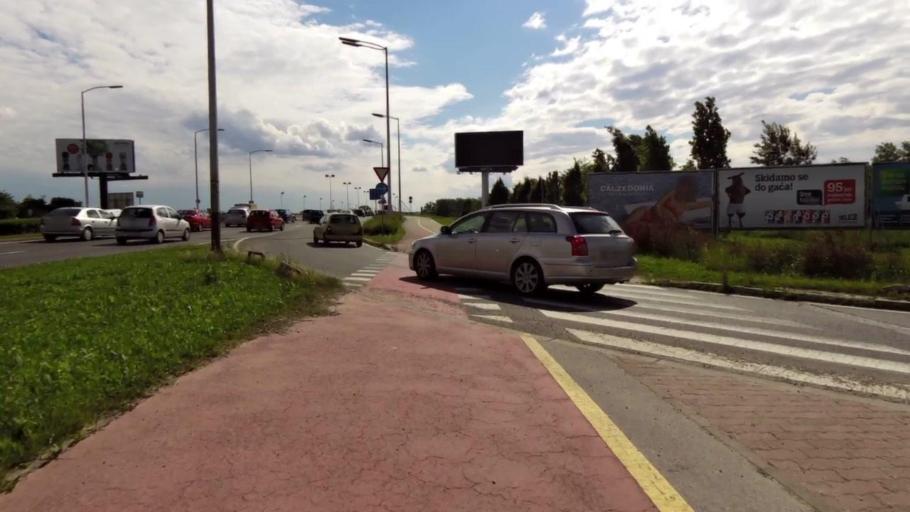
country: HR
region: Grad Zagreb
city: Jezdovec
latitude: 45.7939
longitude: 15.8569
